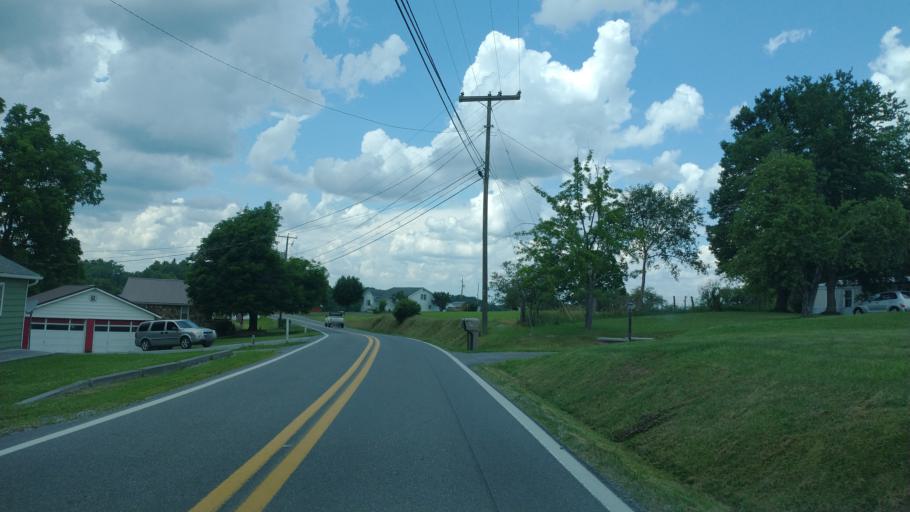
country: US
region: West Virginia
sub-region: Mercer County
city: Athens
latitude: 37.4051
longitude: -81.0590
